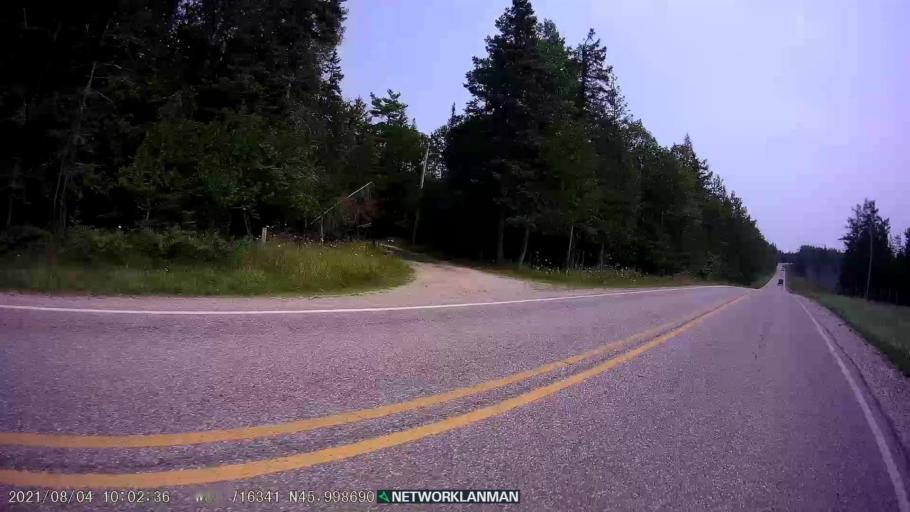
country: CA
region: Ontario
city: Thessalon
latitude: 45.9987
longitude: -83.7157
